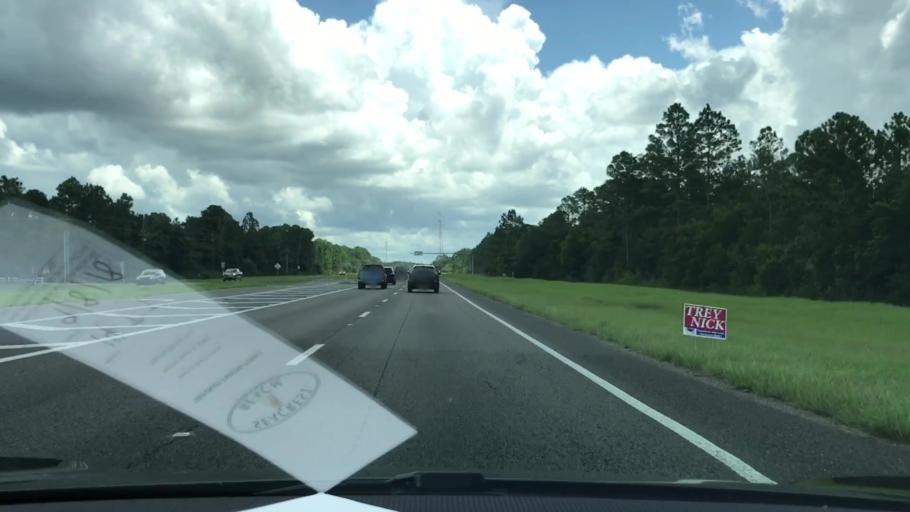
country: US
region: Florida
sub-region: Walton County
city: Seaside
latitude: 30.3579
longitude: -86.1198
